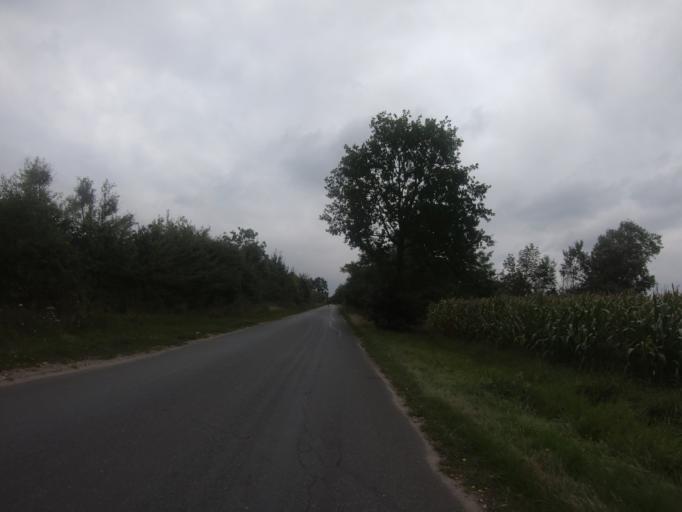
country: DE
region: Lower Saxony
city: Ribbesbuttel
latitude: 52.4394
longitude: 10.5139
